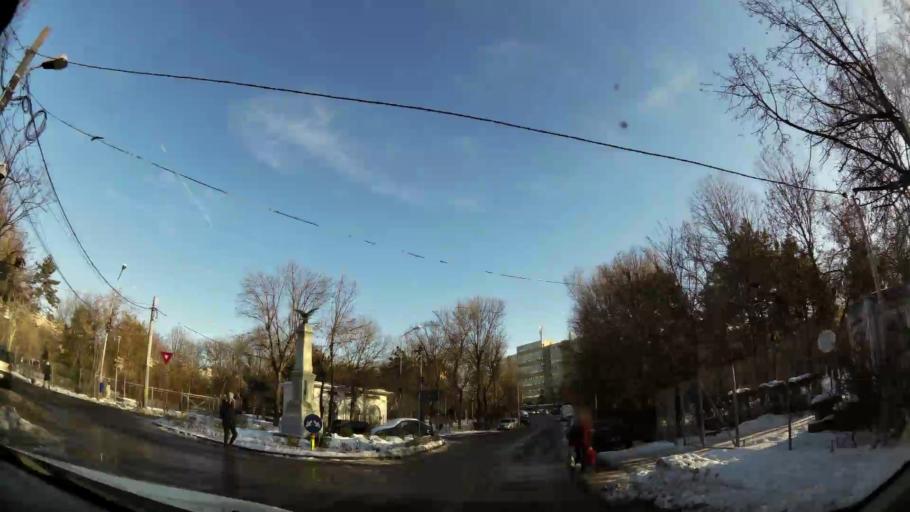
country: RO
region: Ilfov
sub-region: Comuna Fundeni-Dobroesti
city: Fundeni
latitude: 44.4655
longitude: 26.1337
